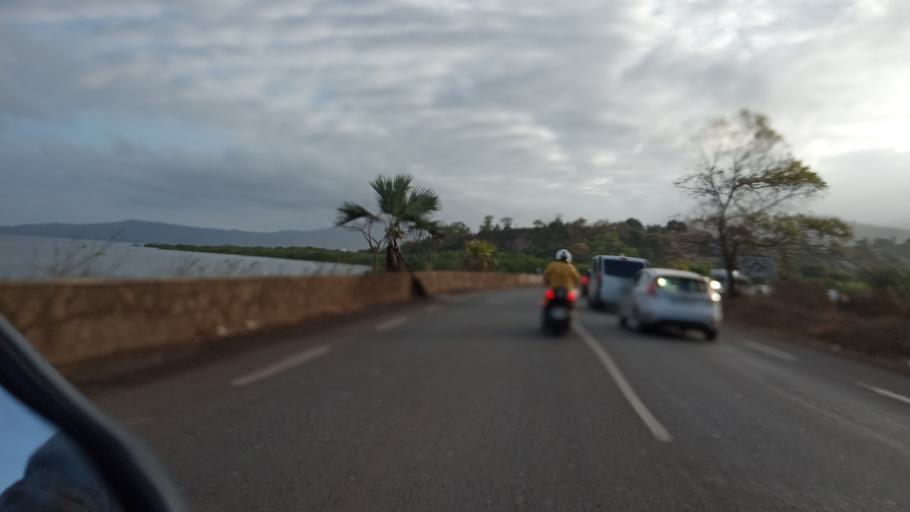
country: YT
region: Mamoudzou
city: Mamoudzou
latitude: -12.7941
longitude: 45.2185
